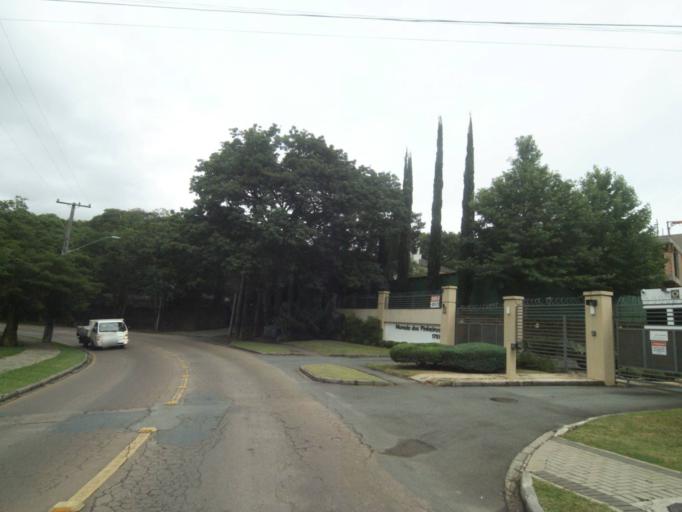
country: BR
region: Parana
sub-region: Curitiba
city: Curitiba
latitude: -25.4498
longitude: -49.3276
